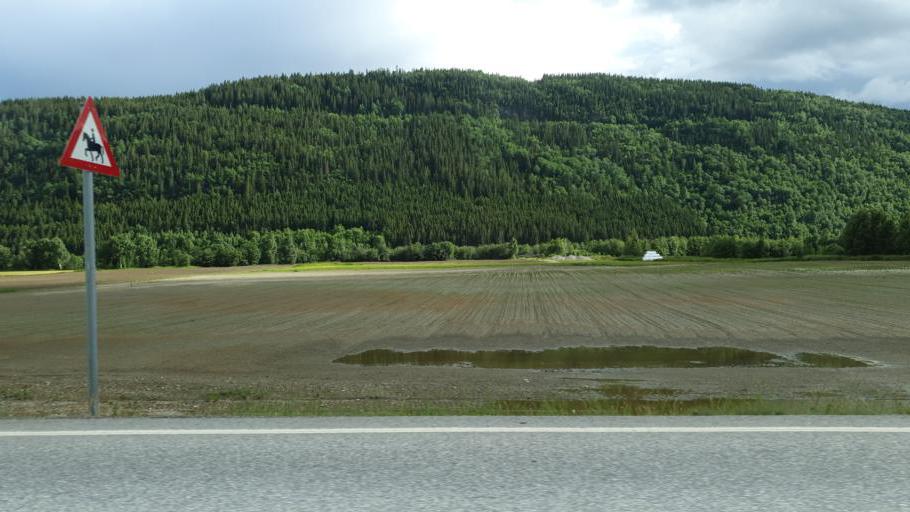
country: NO
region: Oppland
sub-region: Vaga
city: Vagamo
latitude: 61.8759
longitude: 9.1437
